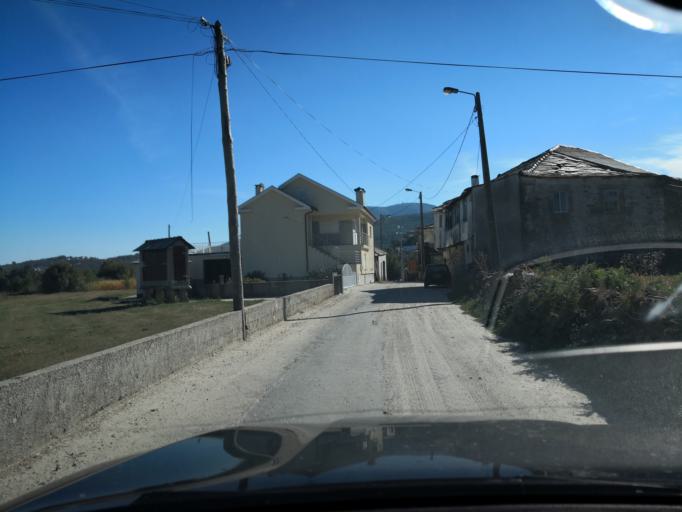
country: PT
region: Vila Real
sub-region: Santa Marta de Penaguiao
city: Santa Marta de Penaguiao
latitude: 41.2995
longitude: -7.8757
